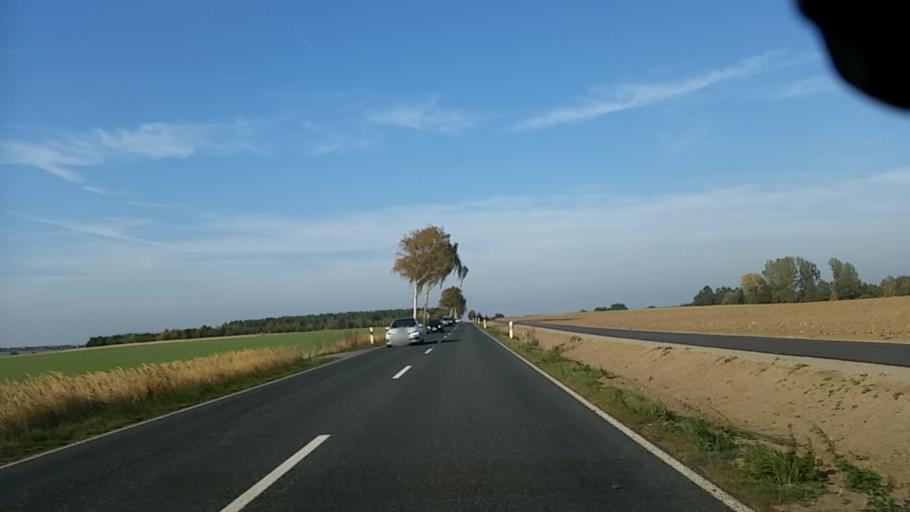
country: DE
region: Lower Saxony
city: Gross Twulpstedt
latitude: 52.3774
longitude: 10.8501
